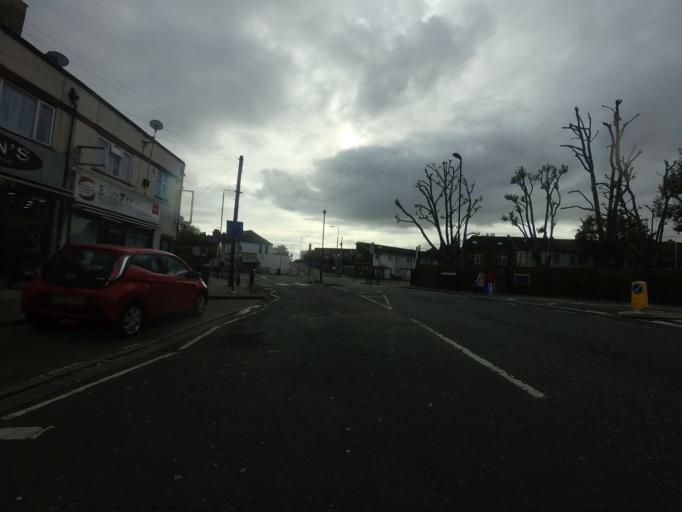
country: GB
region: England
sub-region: Greater London
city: East Ham
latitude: 51.5246
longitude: 0.0394
